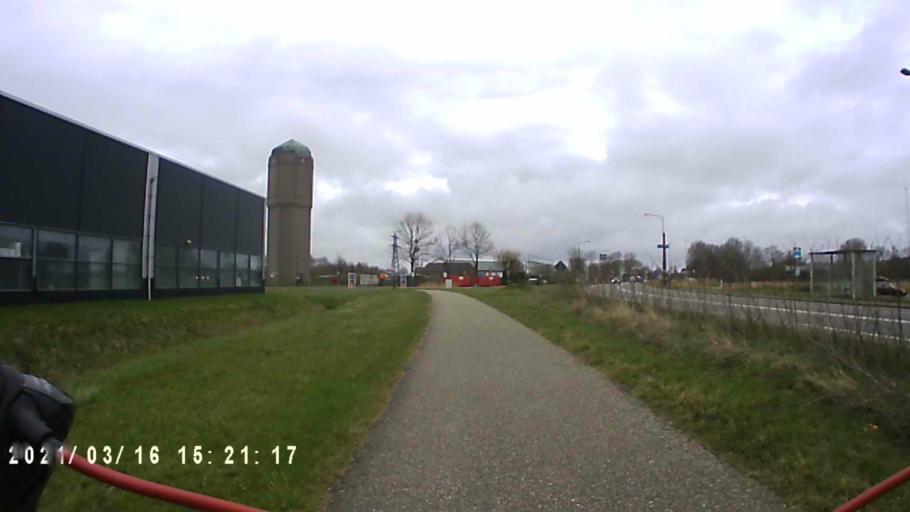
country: NL
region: Friesland
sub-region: Sudwest Fryslan
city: Bolsward
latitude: 53.0634
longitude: 5.5039
